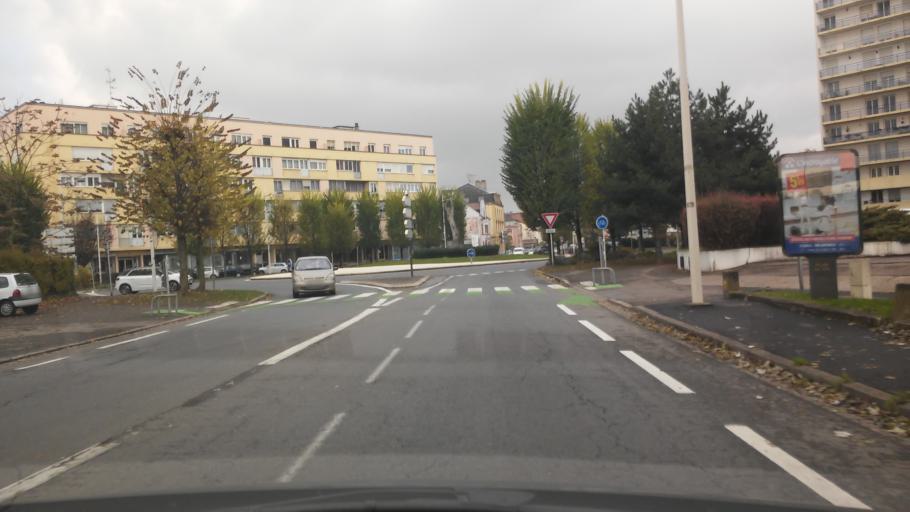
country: FR
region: Lorraine
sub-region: Departement de la Moselle
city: Thionville
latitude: 49.3511
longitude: 6.1603
